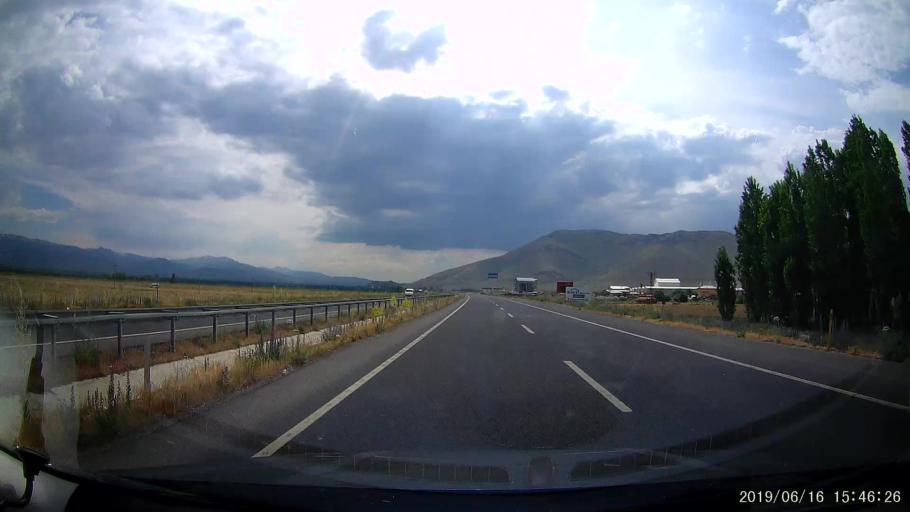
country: TR
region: Erzurum
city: Pasinler
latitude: 39.9901
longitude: 41.7443
